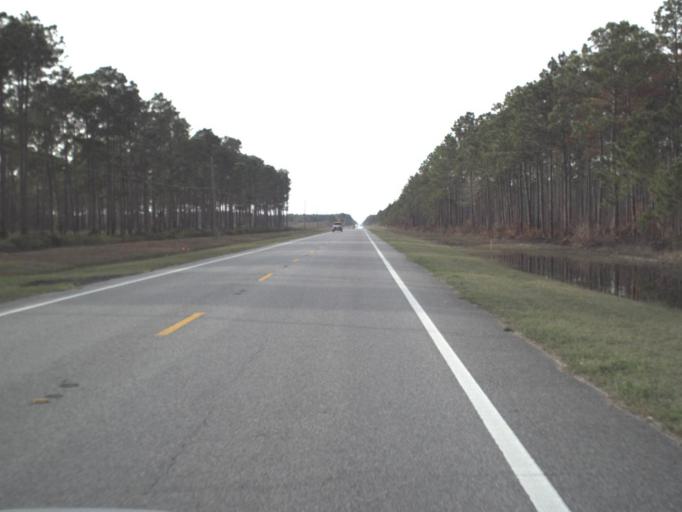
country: US
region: Florida
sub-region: Bay County
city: Tyndall Air Force Base
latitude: 30.0150
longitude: -85.5189
